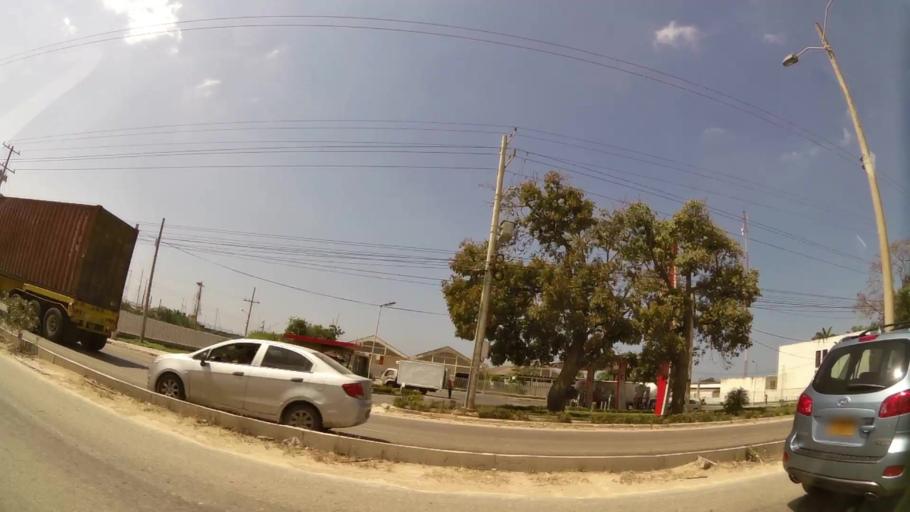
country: CO
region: Bolivar
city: Cartagena
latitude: 10.3631
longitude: -75.5077
